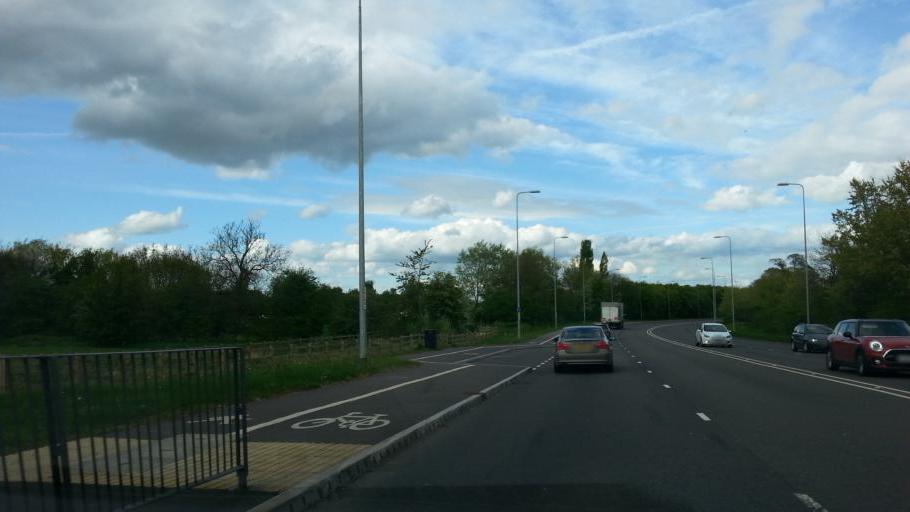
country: GB
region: England
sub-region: Nottinghamshire
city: Gotham
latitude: 52.9011
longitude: -1.1964
